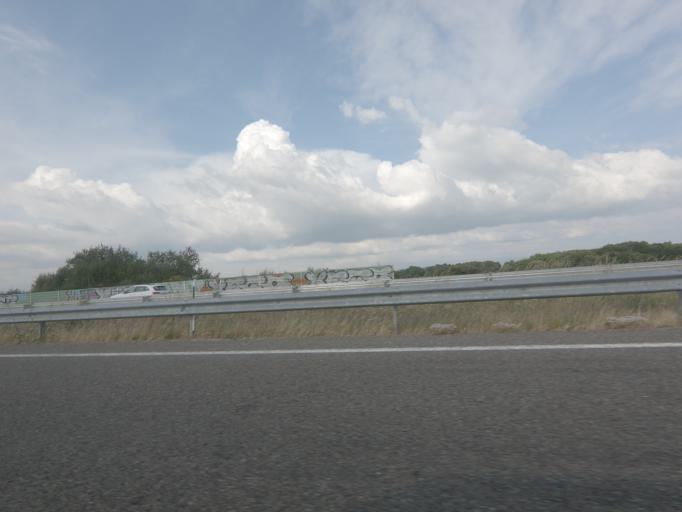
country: ES
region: Galicia
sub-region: Provincia de Ourense
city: Ambia
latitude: 42.1359
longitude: -7.7436
